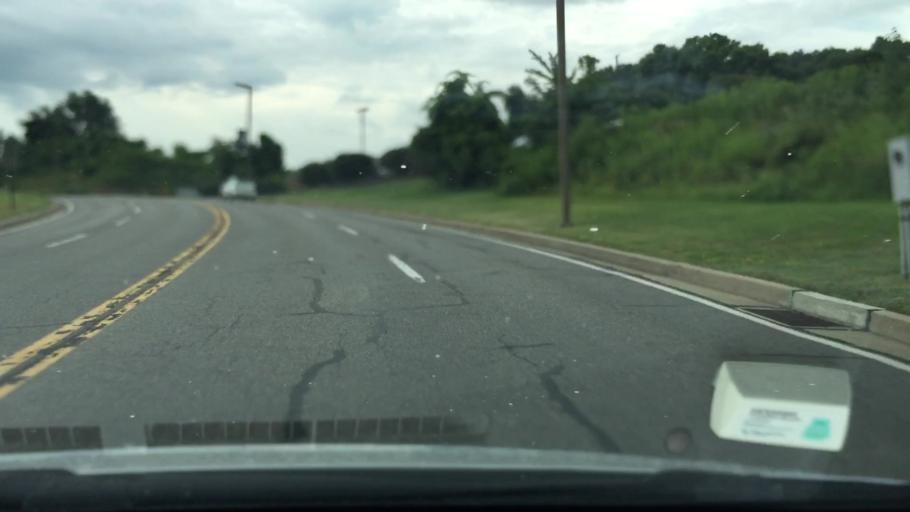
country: US
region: Pennsylvania
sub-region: Allegheny County
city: Enlow
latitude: 40.4511
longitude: -80.1921
